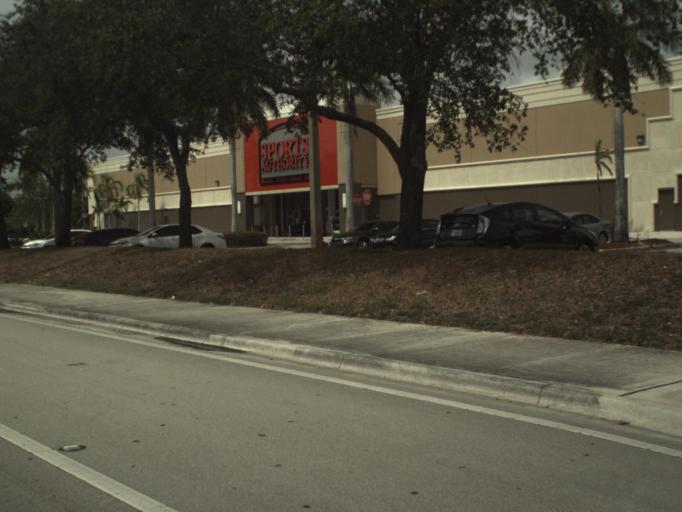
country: US
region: Florida
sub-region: Broward County
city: Sunrise
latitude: 26.1538
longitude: -80.1186
